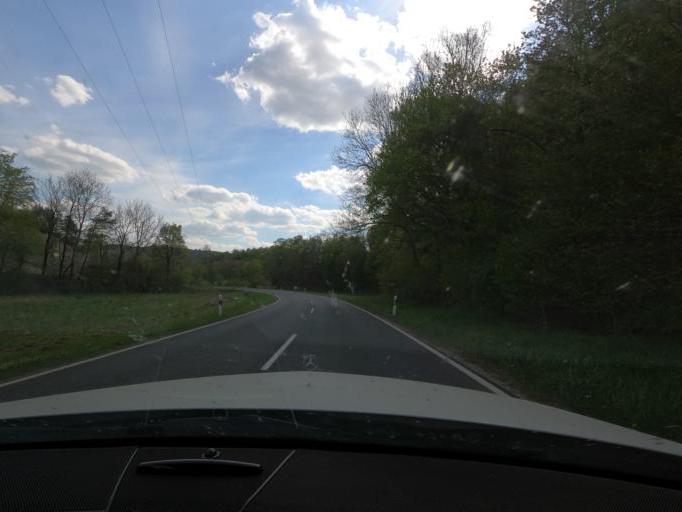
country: DE
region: Hesse
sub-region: Regierungsbezirk Kassel
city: Weissenborn
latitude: 51.1140
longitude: 10.0544
